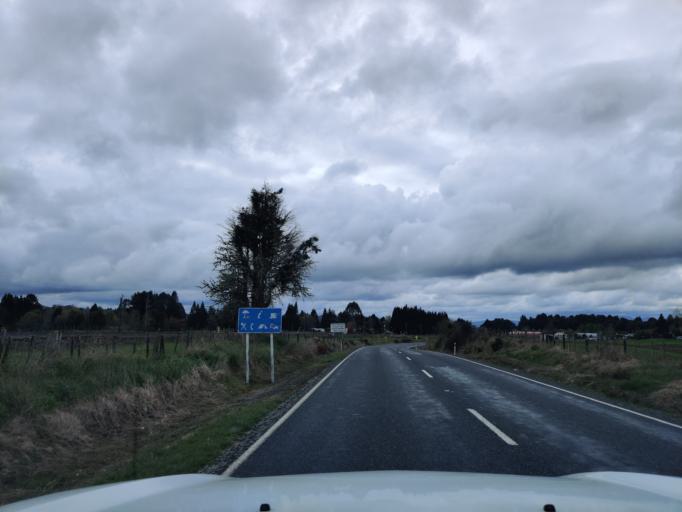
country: NZ
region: Waikato
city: Turangi
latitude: -39.0052
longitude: 175.3768
